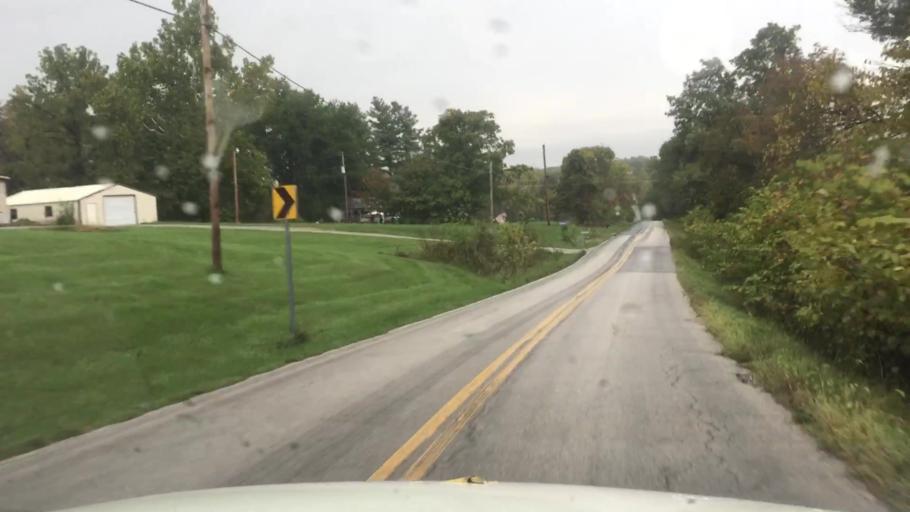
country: US
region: Missouri
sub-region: Boone County
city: Columbia
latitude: 38.9342
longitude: -92.4965
